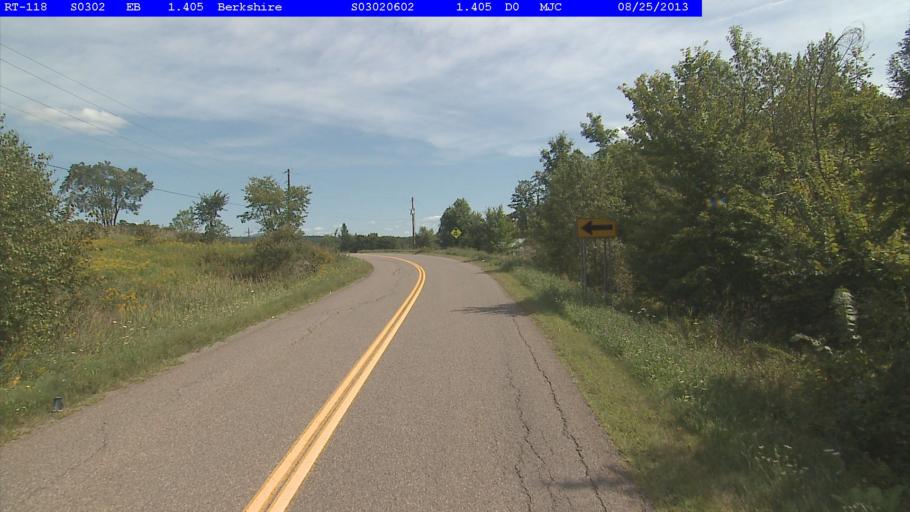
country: US
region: Vermont
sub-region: Franklin County
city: Enosburg Falls
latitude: 44.9803
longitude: -72.7888
